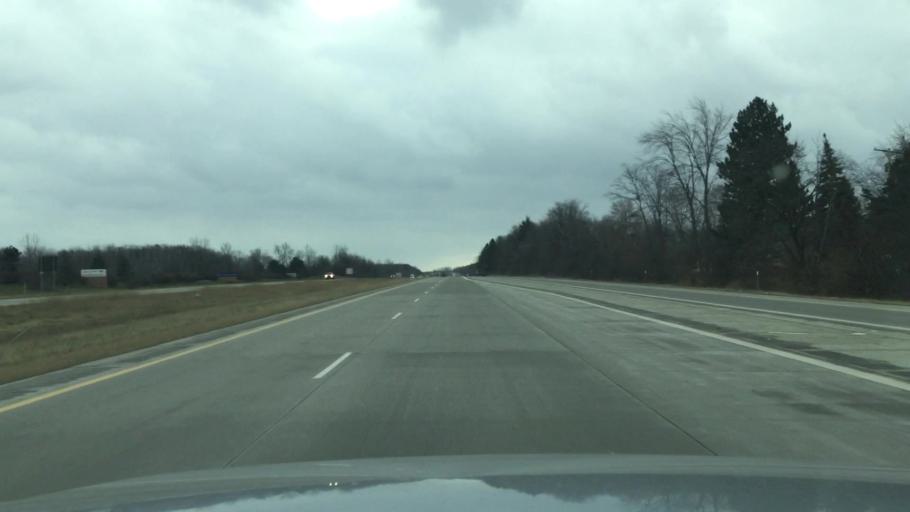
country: US
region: Michigan
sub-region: Genesee County
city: Grand Blanc
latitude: 42.9412
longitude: -83.6817
